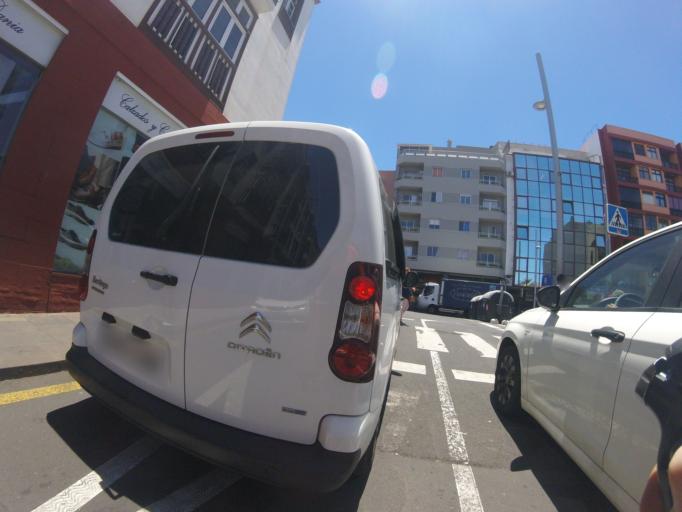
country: ES
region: Canary Islands
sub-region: Provincia de Santa Cruz de Tenerife
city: La Laguna
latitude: 28.4868
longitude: -16.3162
